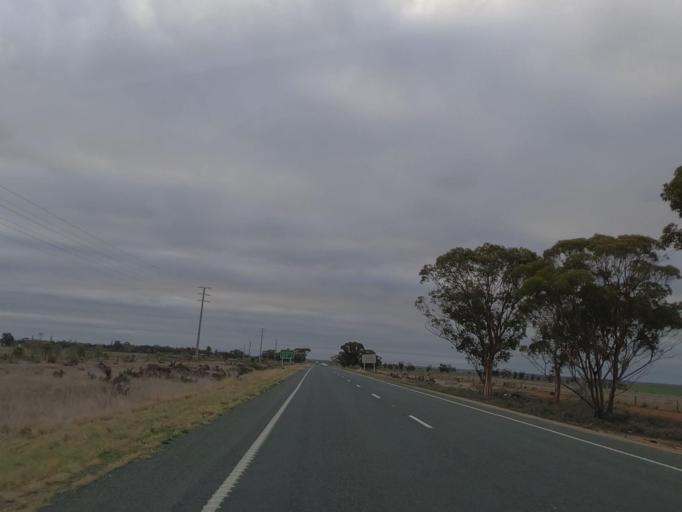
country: AU
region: Victoria
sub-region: Swan Hill
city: Swan Hill
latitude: -35.5682
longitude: 143.7849
